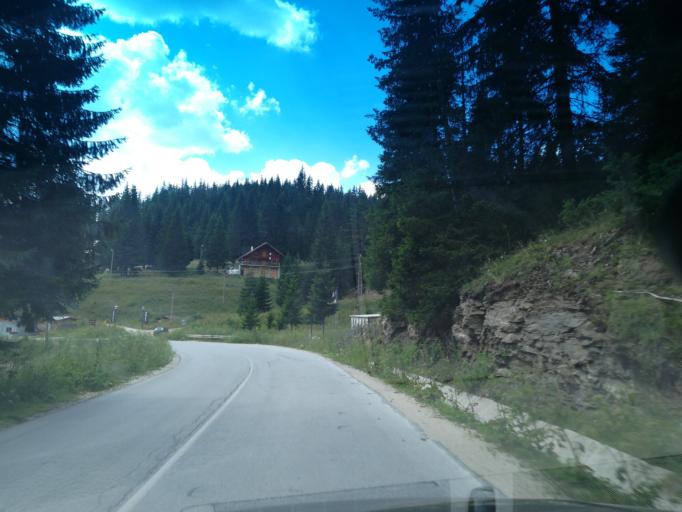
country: BG
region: Smolyan
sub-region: Obshtina Chepelare
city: Chepelare
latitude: 41.6618
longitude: 24.6796
